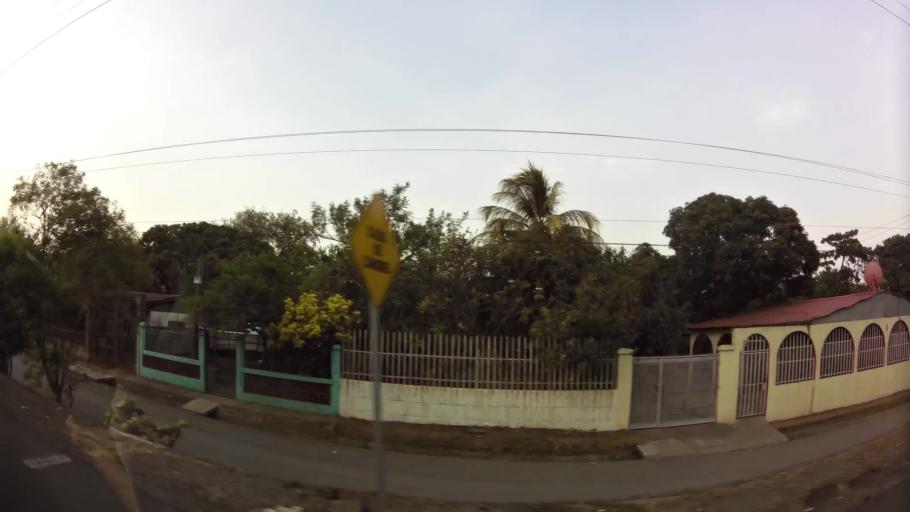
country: NI
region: Managua
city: Ciudad Sandino
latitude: 12.1879
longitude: -86.3648
